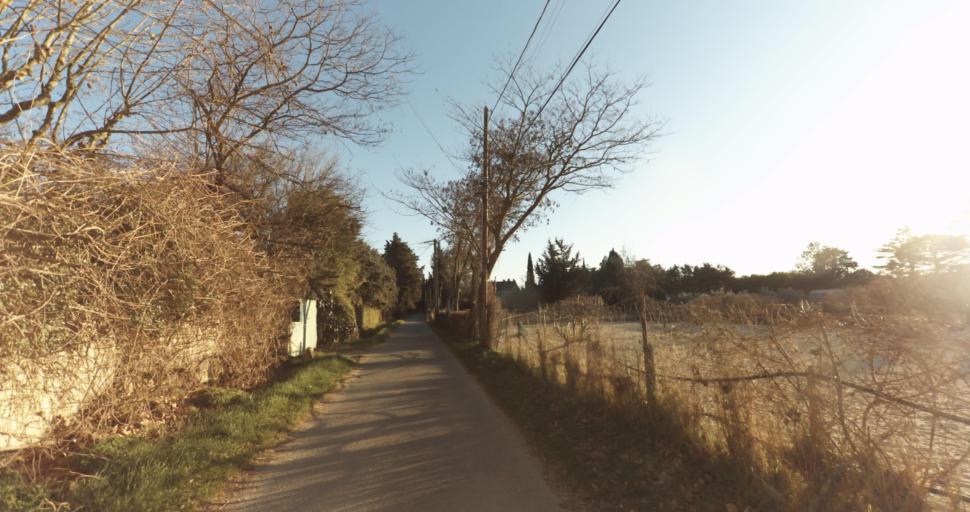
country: FR
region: Provence-Alpes-Cote d'Azur
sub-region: Departement des Bouches-du-Rhone
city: Barbentane
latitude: 43.9128
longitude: 4.7709
